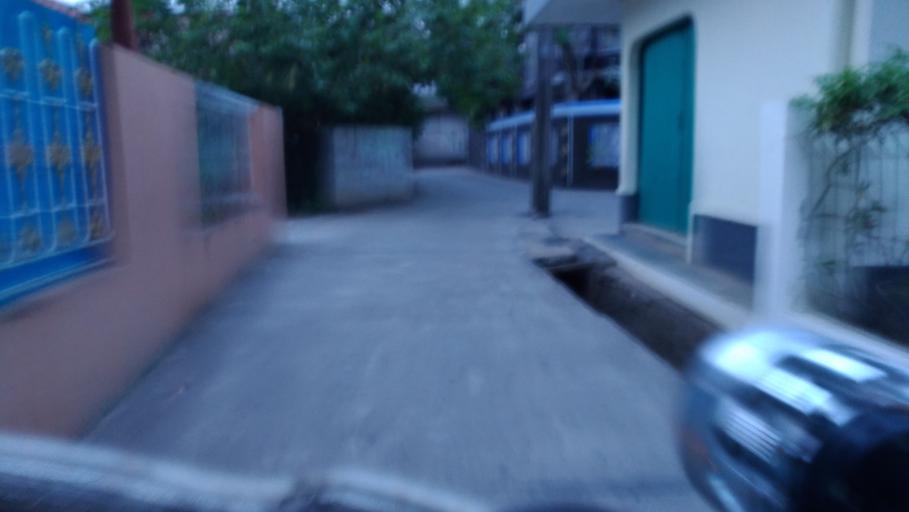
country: ID
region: West Java
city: Depok
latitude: -6.3532
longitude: 106.8769
